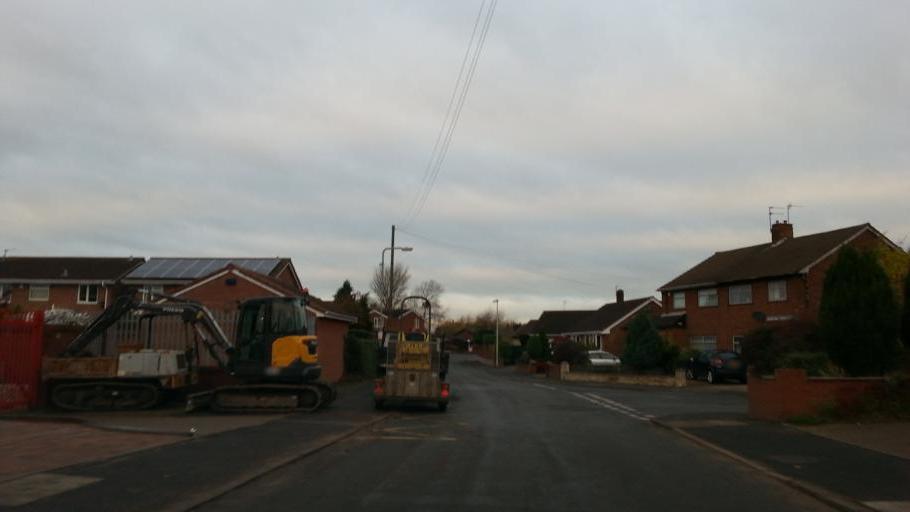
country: GB
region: England
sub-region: Sandwell
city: Wednesbury
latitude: 52.5461
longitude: -2.0409
